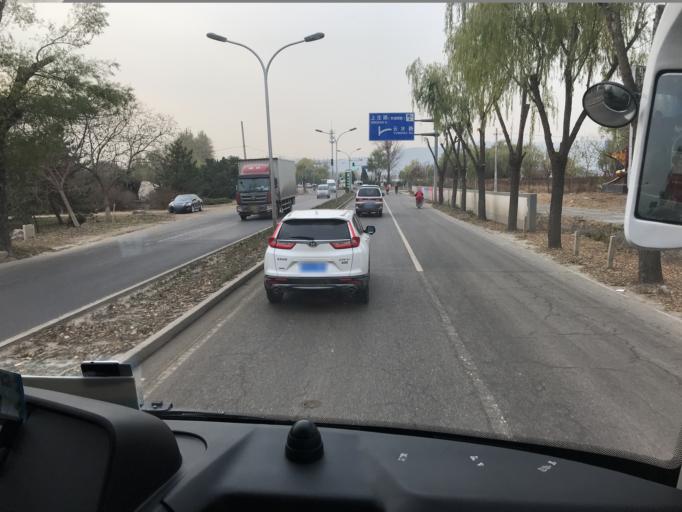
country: CN
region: Beijing
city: Wenquan
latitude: 40.0802
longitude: 116.2105
